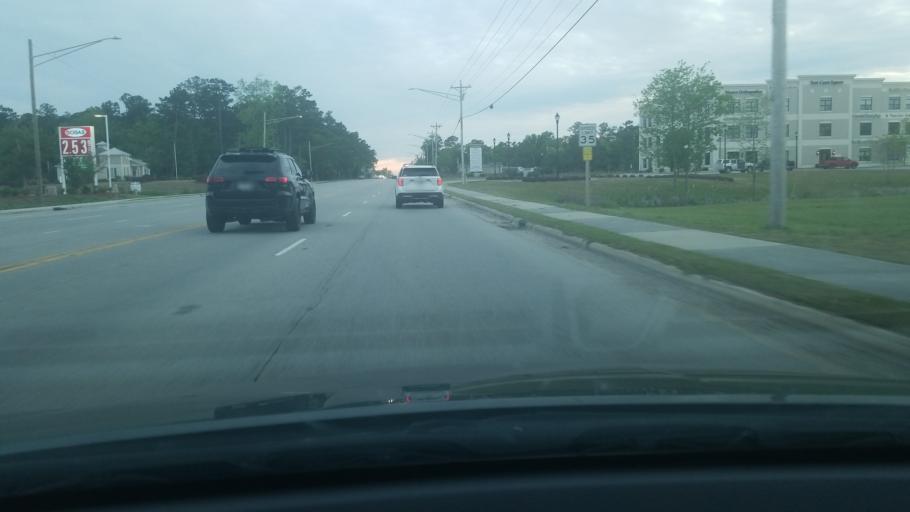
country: US
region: North Carolina
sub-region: Carteret County
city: Cedar Point
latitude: 34.6875
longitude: -77.0729
